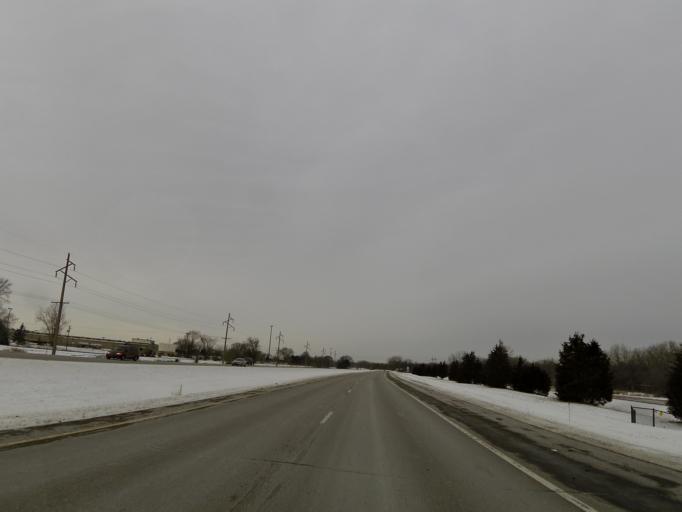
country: US
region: Minnesota
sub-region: Scott County
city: Shakopee
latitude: 44.8012
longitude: -93.4755
